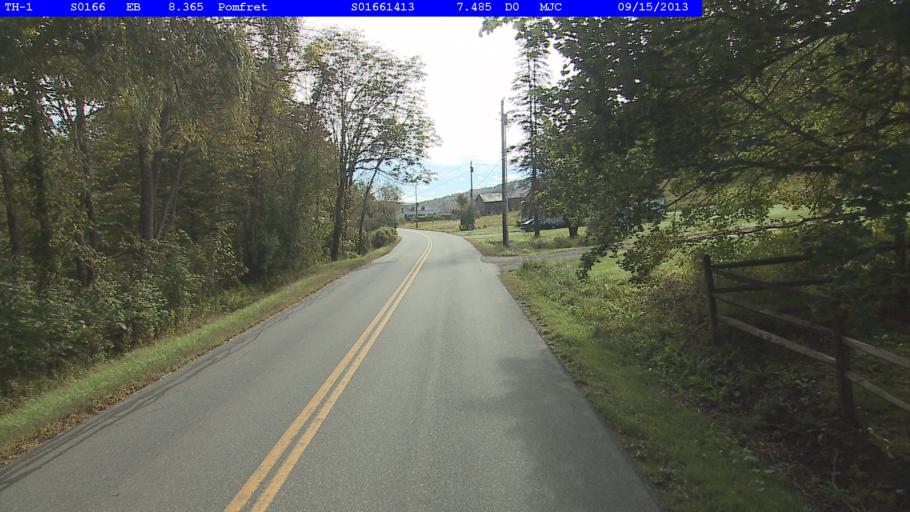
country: US
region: Vermont
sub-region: Windsor County
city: Woodstock
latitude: 43.7259
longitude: -72.4735
